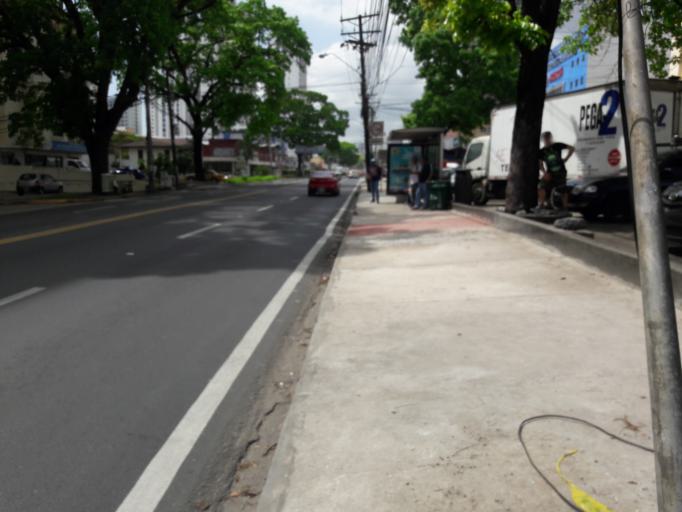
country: PA
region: Panama
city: Panama
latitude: 9.0081
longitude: -79.5079
